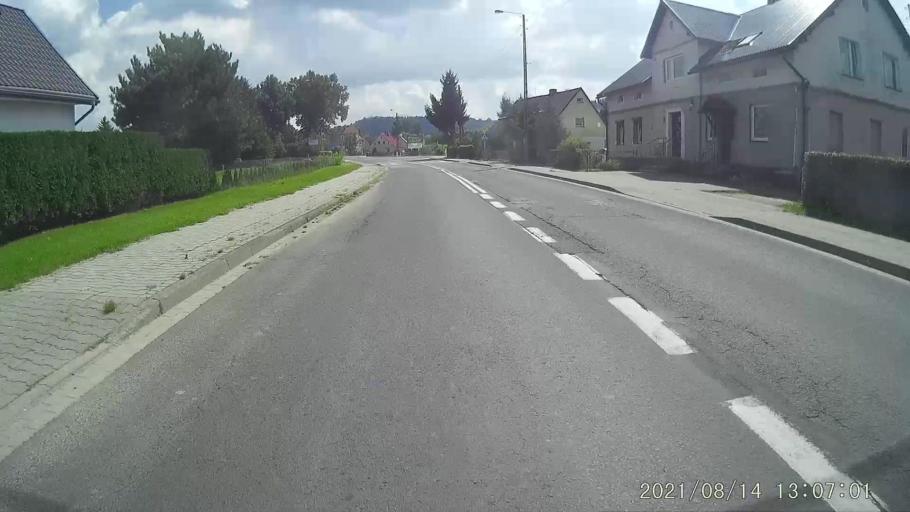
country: PL
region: Lower Silesian Voivodeship
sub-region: Powiat klodzki
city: Klodzko
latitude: 50.3648
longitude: 16.7115
